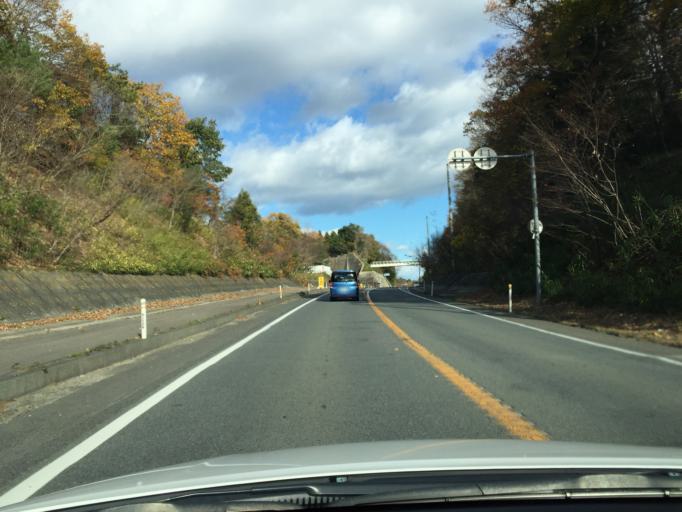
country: JP
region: Fukushima
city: Namie
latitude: 37.5056
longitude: 140.9971
